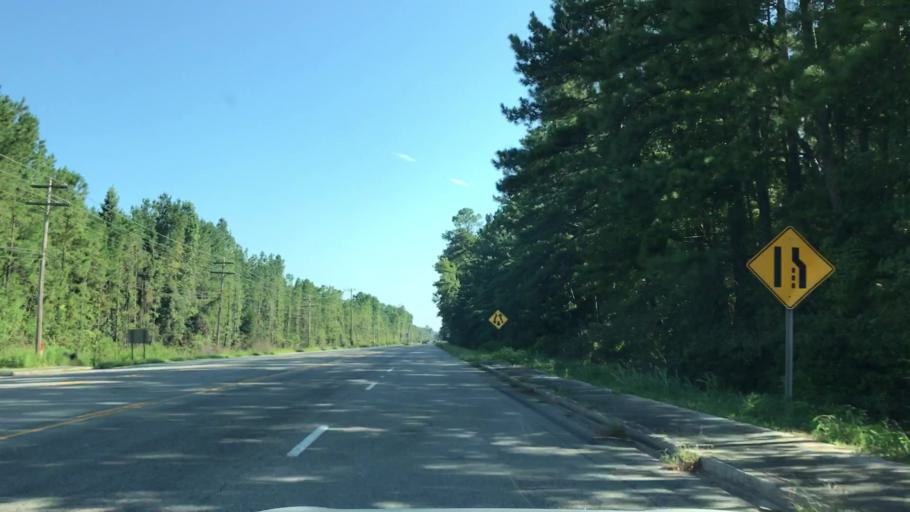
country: US
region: South Carolina
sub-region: Georgetown County
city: Georgetown
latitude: 33.4181
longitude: -79.2835
